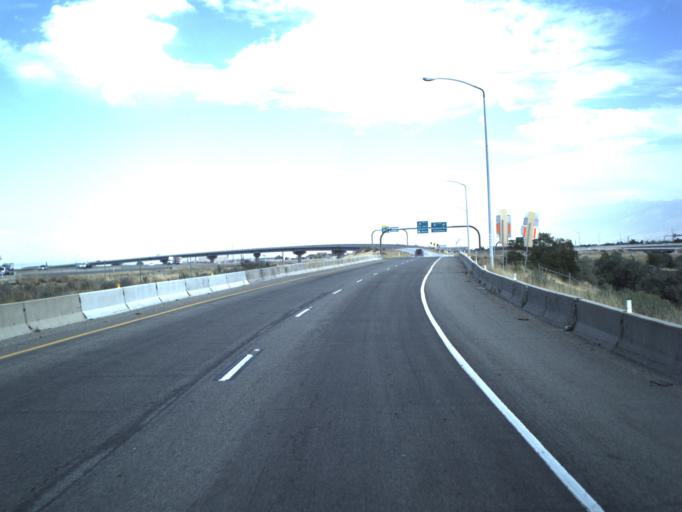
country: US
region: Utah
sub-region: Salt Lake County
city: Salt Lake City
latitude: 40.7593
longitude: -111.9501
